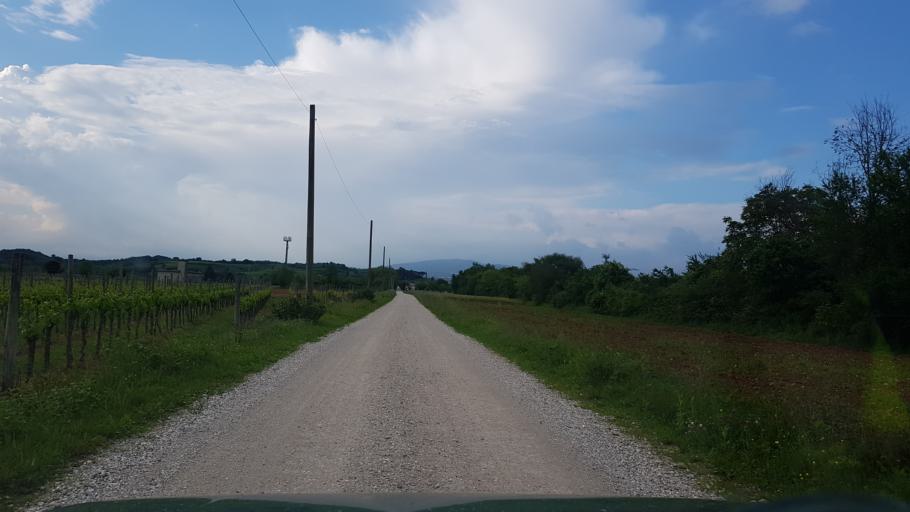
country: IT
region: Friuli Venezia Giulia
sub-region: Provincia di Gorizia
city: Mossa
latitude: 45.9260
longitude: 13.5426
